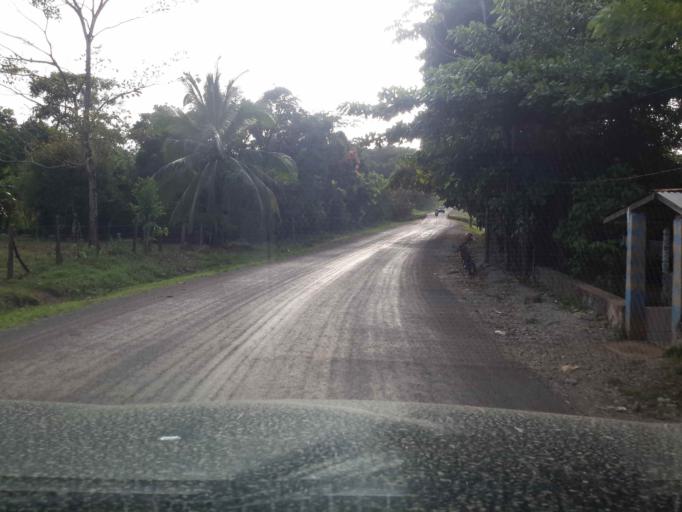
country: CR
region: Alajuela
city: Los Chiles
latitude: 11.1508
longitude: -84.6377
